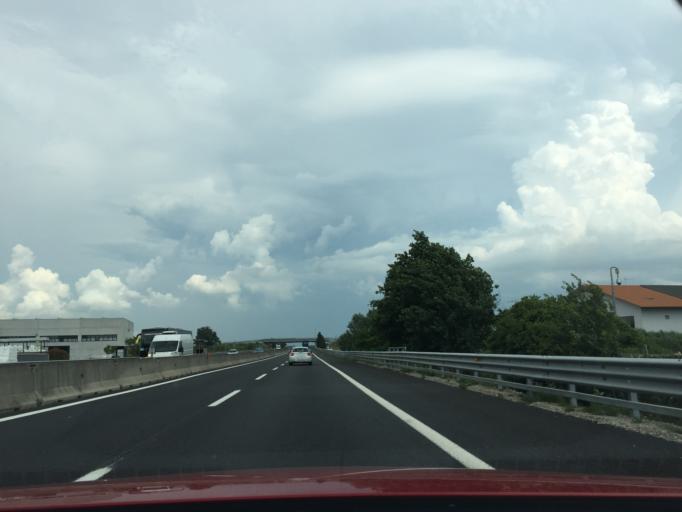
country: IT
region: Tuscany
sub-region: Provincia di Lucca
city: Porcari
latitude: 43.8200
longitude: 10.6188
